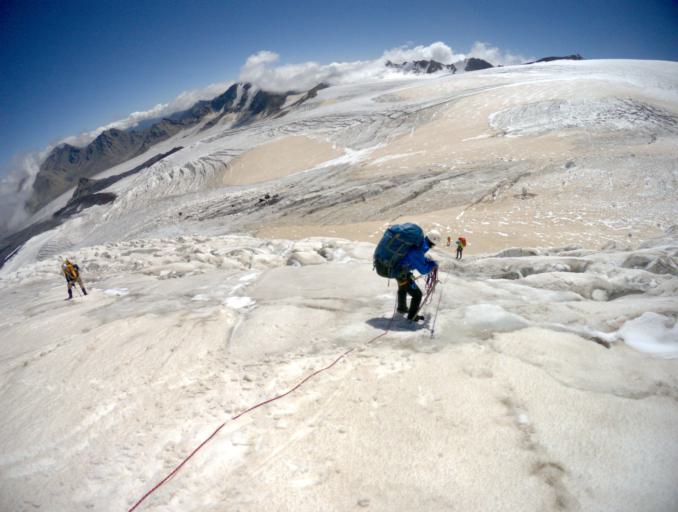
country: RU
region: Kabardino-Balkariya
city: Terskol
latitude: 43.3590
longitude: 42.4988
